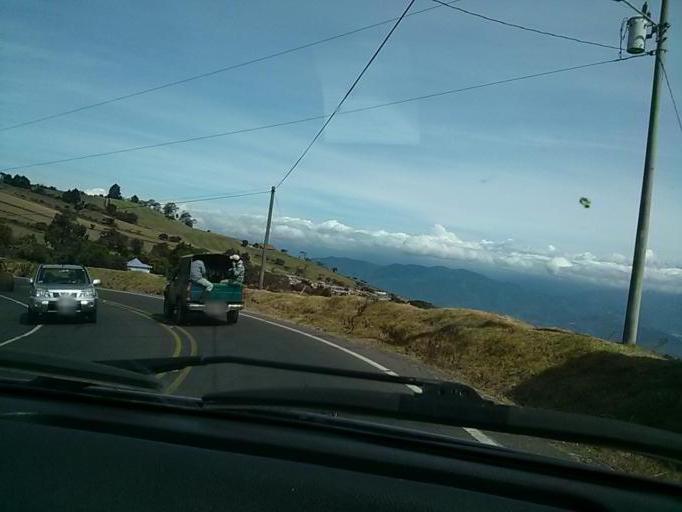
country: CR
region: Cartago
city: Cot
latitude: 9.9235
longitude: -83.8817
